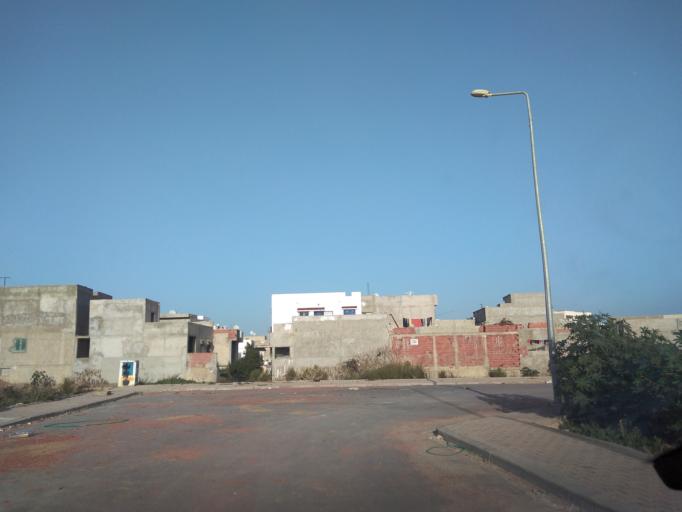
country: TN
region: Manouba
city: Manouba
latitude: 36.7967
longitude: 10.0869
